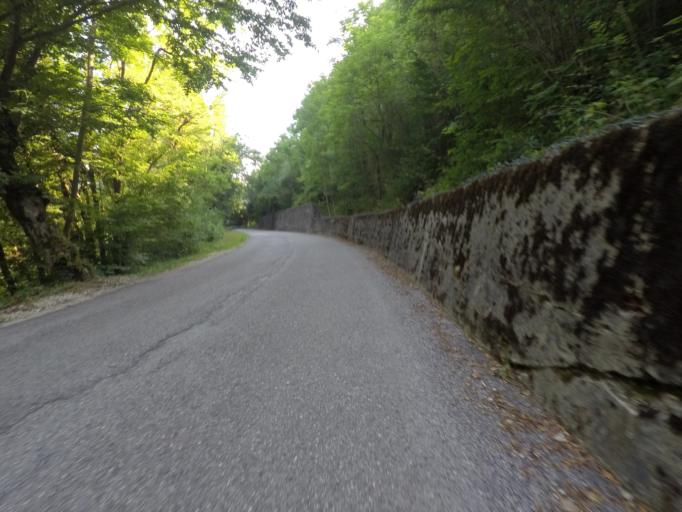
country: IT
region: Friuli Venezia Giulia
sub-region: Provincia di Udine
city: Nimis
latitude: 46.1768
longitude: 13.2593
